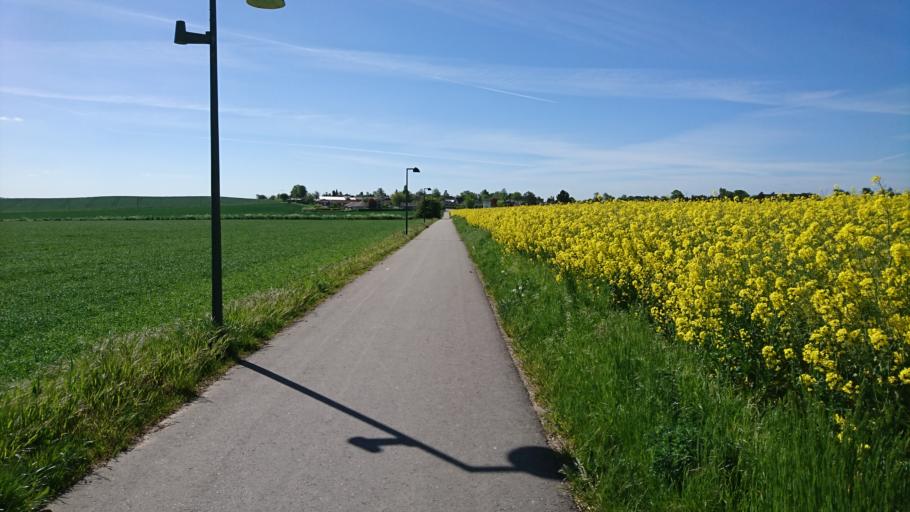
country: DK
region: Capital Region
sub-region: Egedal Kommune
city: Olstykke
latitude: 55.8046
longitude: 12.1165
